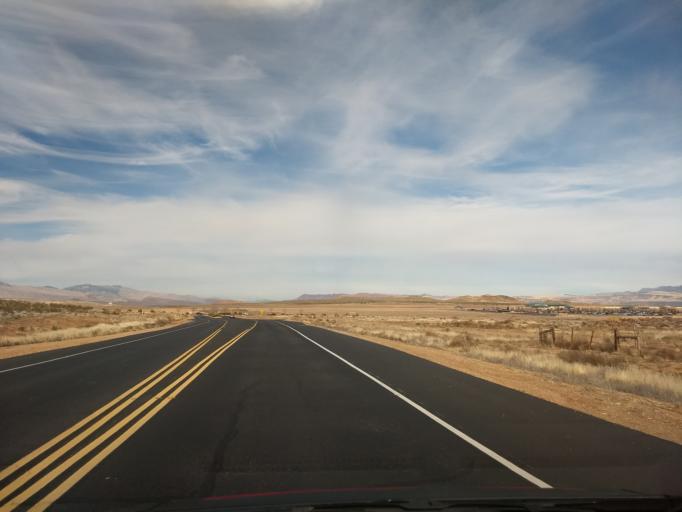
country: US
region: Utah
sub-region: Washington County
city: Washington
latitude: 37.0227
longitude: -113.5053
